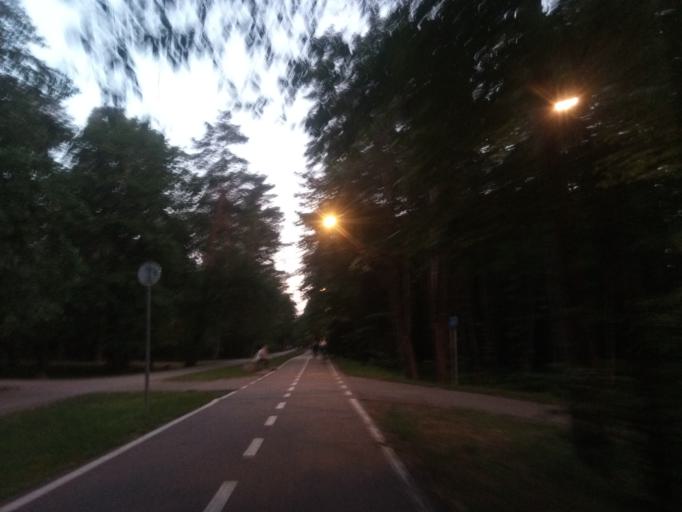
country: LT
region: Vilnius County
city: Vilkpede
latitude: 54.6893
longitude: 25.2384
